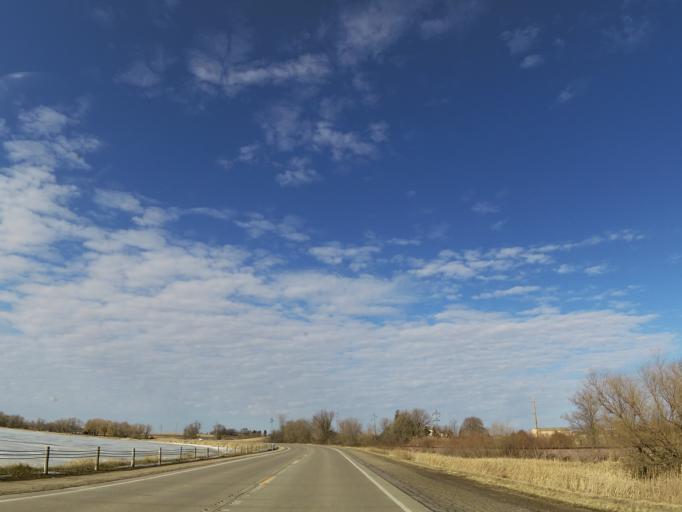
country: US
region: Minnesota
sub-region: Le Sueur County
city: Montgomery
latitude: 44.4758
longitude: -93.5824
